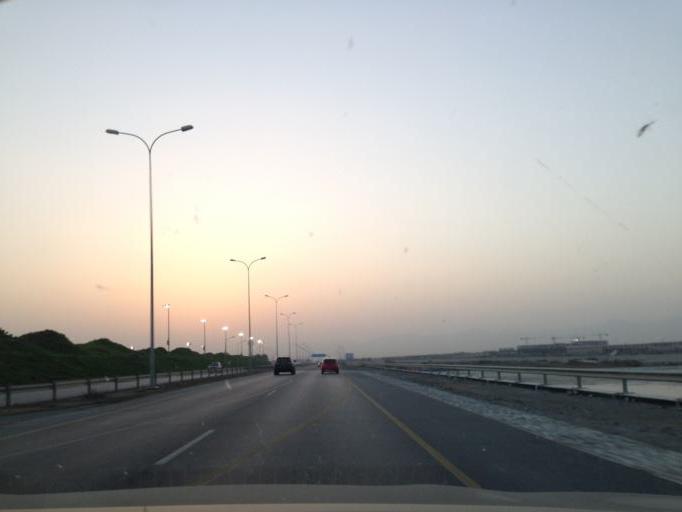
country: OM
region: Muhafazat Masqat
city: Bawshar
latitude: 23.6128
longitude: 58.2975
